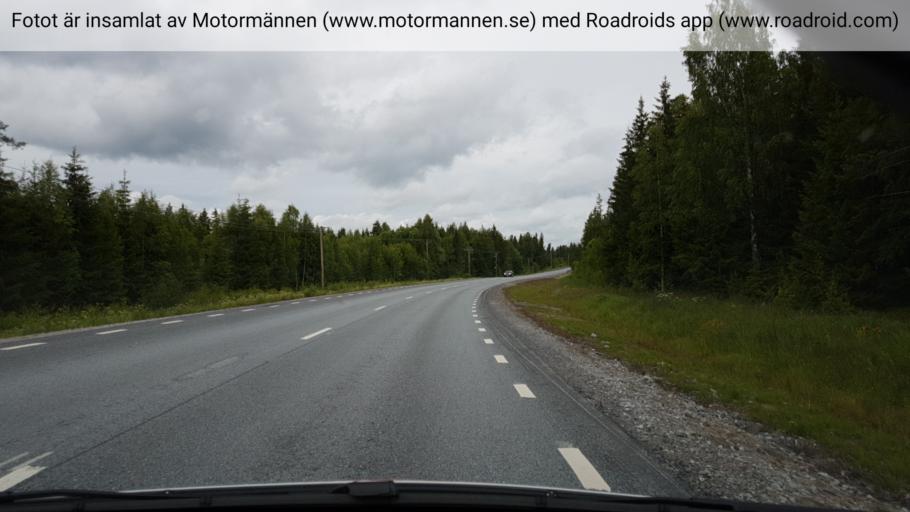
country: SE
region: Vaesternorrland
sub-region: Solleftea Kommun
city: Solleftea
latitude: 63.3628
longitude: 17.0151
